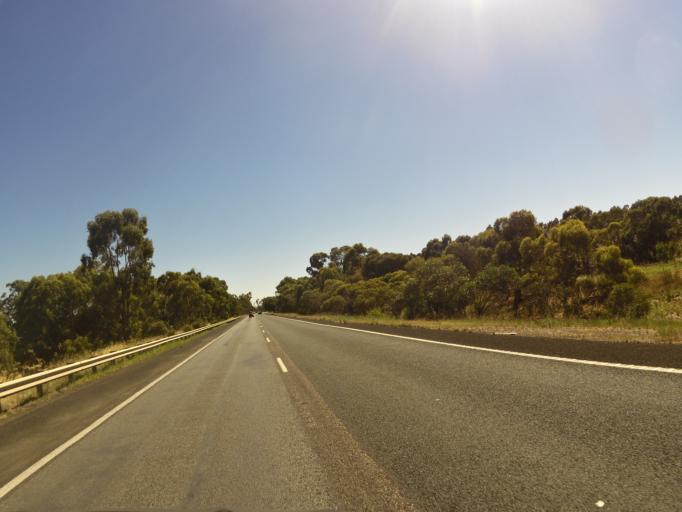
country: AU
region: Victoria
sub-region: Greater Shepparton
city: Shepparton
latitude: -36.8846
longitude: 145.2656
